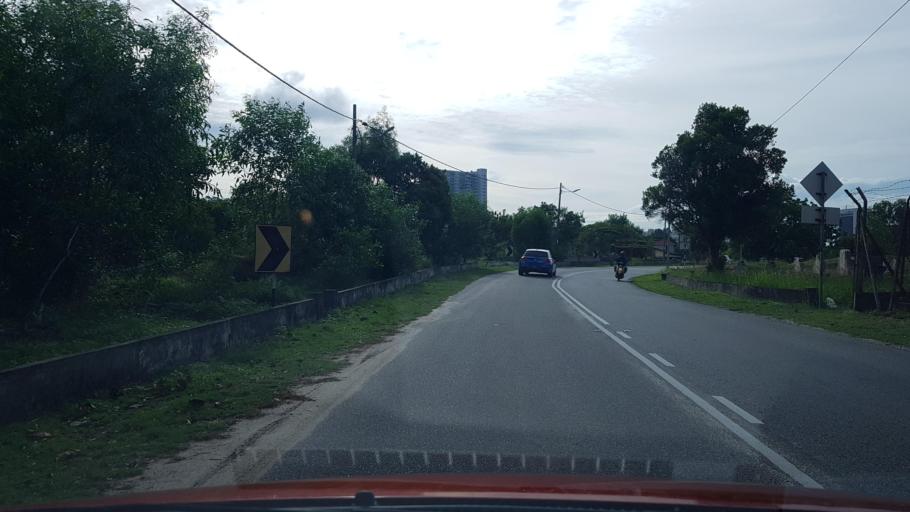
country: MY
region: Terengganu
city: Kuala Terengganu
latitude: 5.3188
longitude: 103.1479
